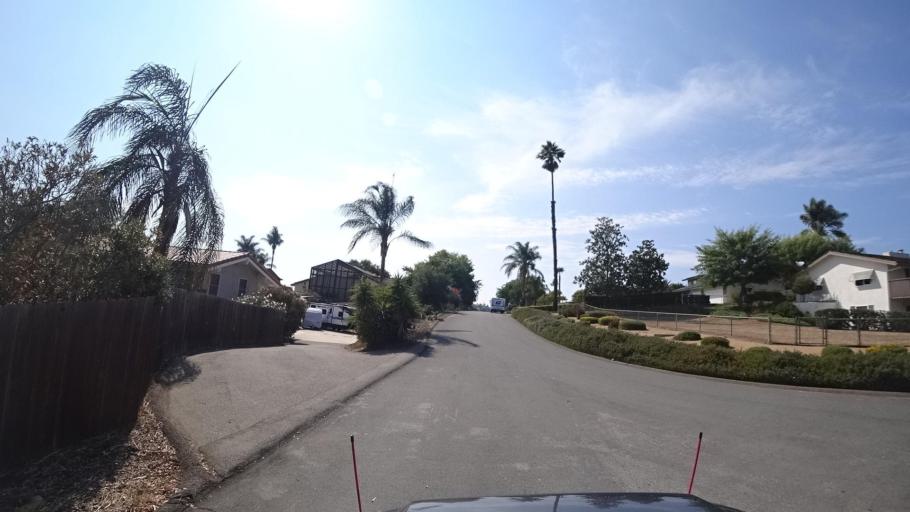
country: US
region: California
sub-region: San Diego County
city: Escondido
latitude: 33.1138
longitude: -117.0527
